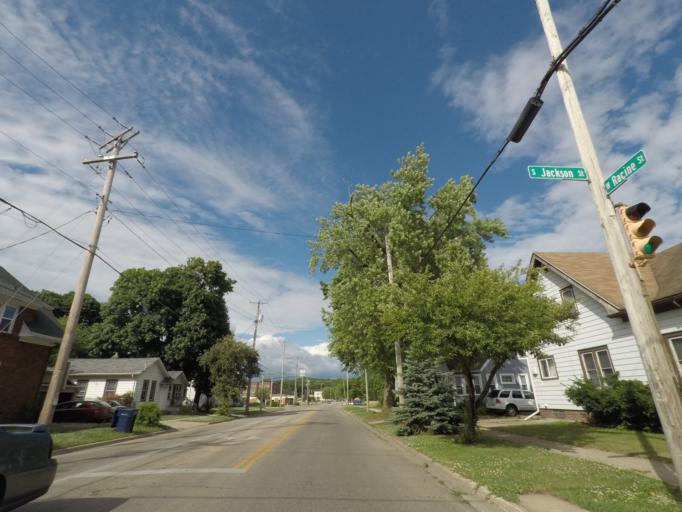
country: US
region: Wisconsin
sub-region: Rock County
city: Janesville
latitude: 42.6749
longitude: -89.0206
